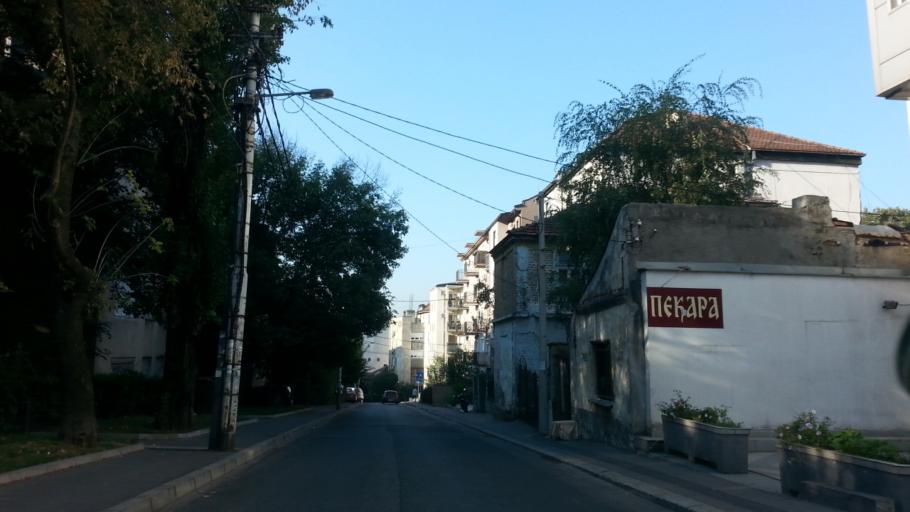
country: RS
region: Central Serbia
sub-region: Belgrade
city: Vracar
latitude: 44.7946
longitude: 20.4977
